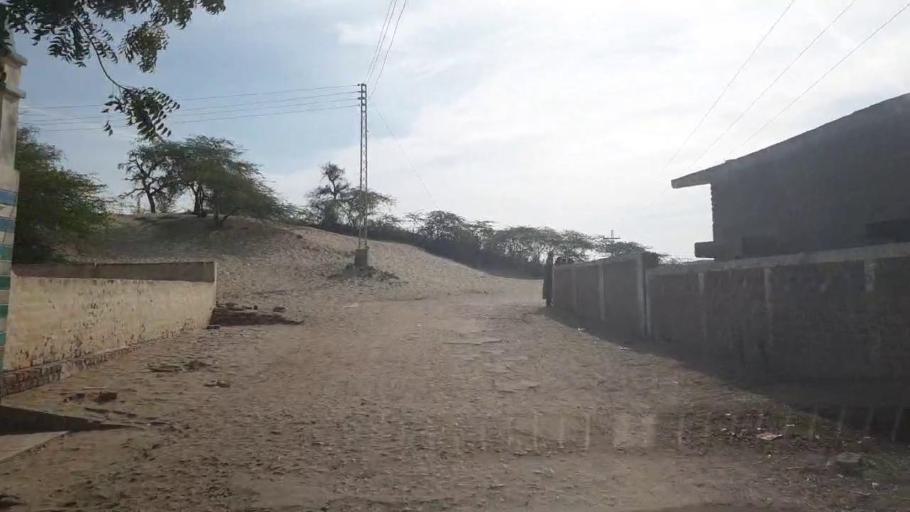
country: PK
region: Sindh
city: Umarkot
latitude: 25.3065
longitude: 69.7019
